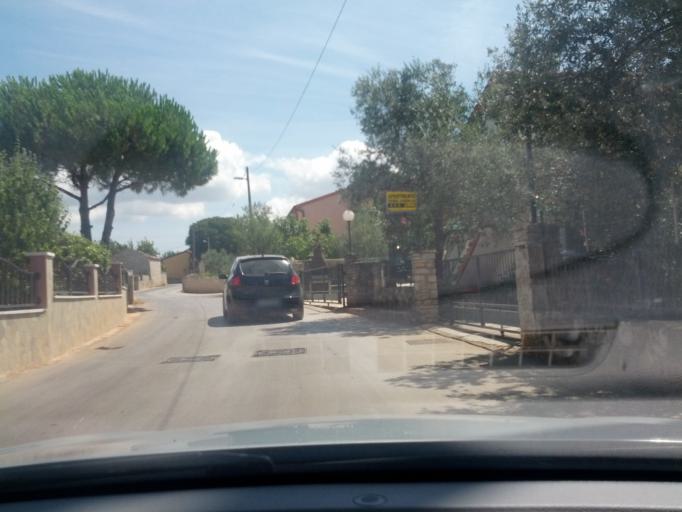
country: HR
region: Istarska
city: Fazana
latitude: 44.9527
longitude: 13.7946
